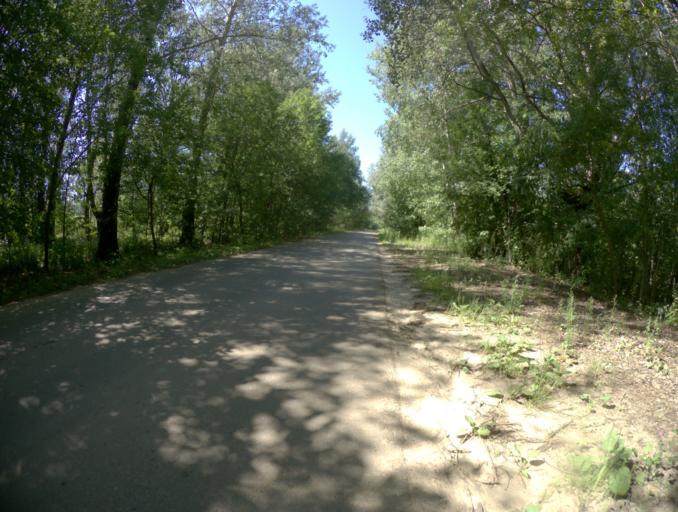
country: RU
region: Nizjnij Novgorod
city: Gorbatov
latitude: 56.1221
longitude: 43.1151
